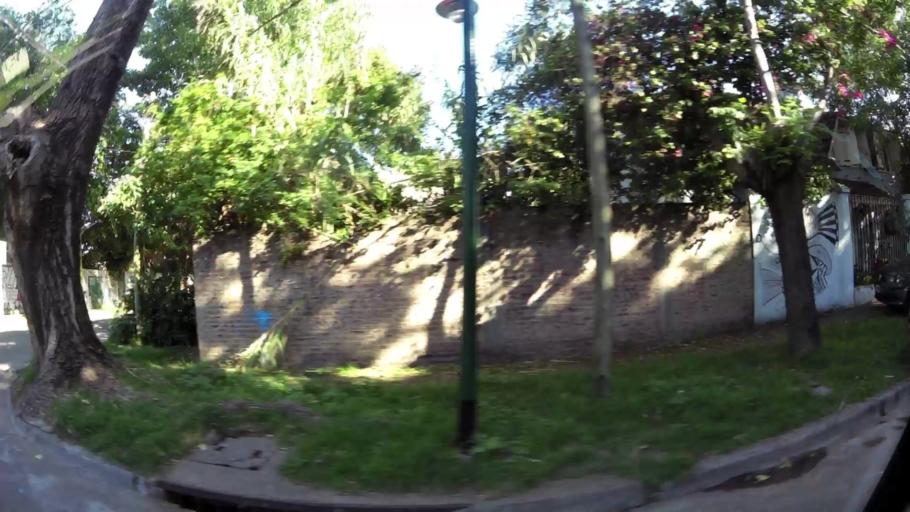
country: AR
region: Buenos Aires
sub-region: Partido de San Isidro
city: San Isidro
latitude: -34.4674
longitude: -58.5022
